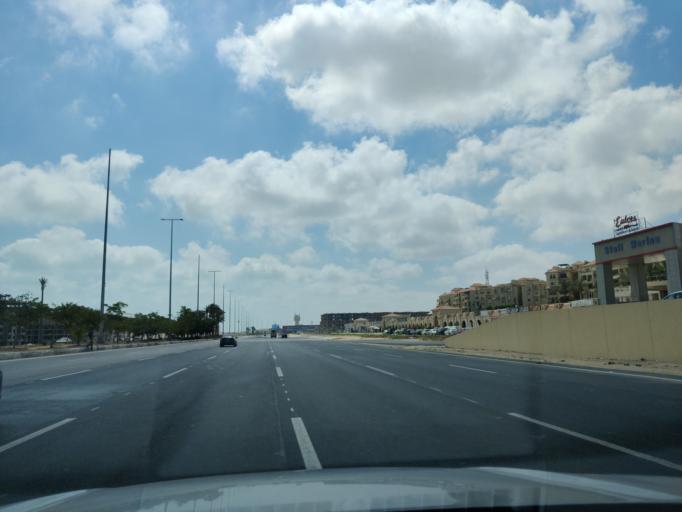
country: EG
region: Muhafazat Matruh
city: Al `Alamayn
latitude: 30.8457
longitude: 28.9339
